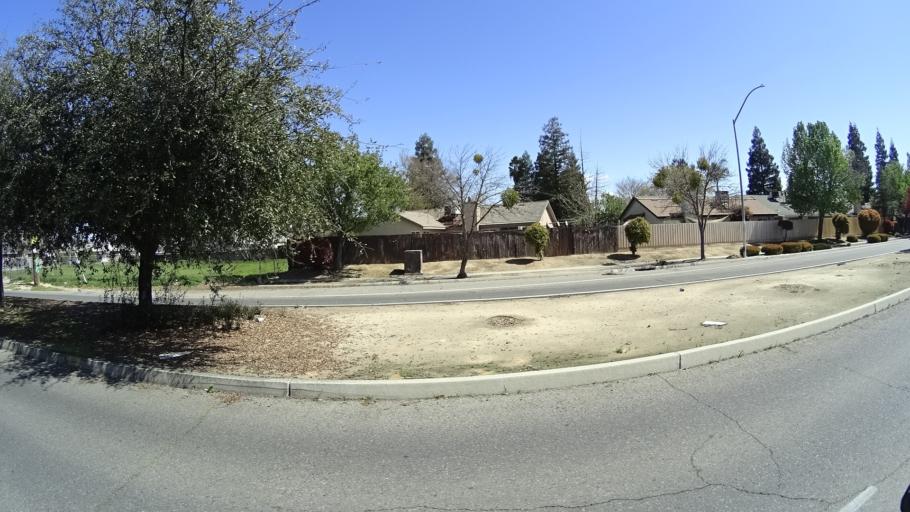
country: US
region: California
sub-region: Fresno County
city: West Park
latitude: 36.7732
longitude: -119.8714
